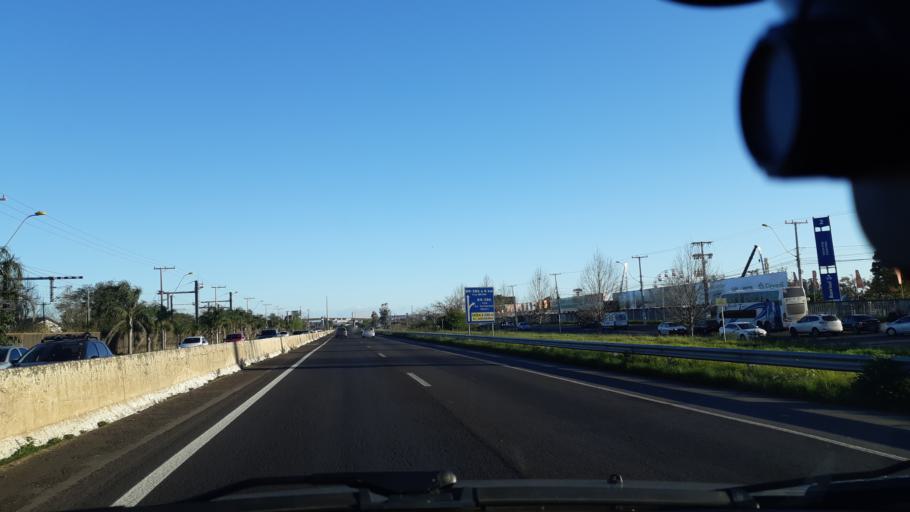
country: BR
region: Rio Grande do Sul
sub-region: Esteio
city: Esteio
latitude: -29.8548
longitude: -51.1802
